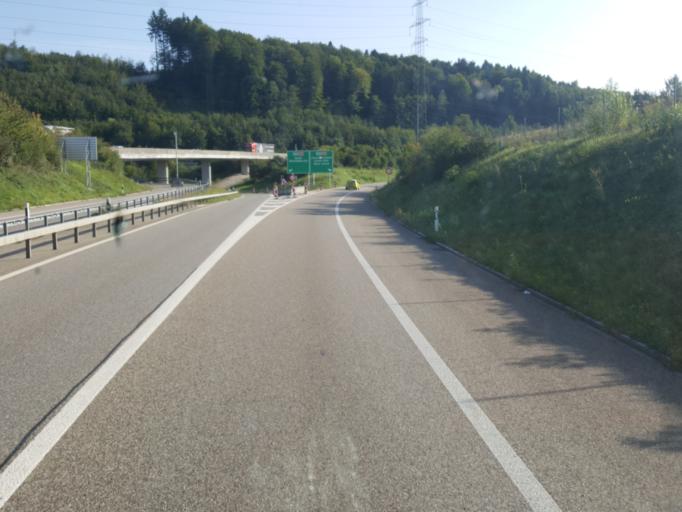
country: CH
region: Basel-Landschaft
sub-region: Bezirk Liestal
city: Arisdorf
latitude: 47.5434
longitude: 7.7589
